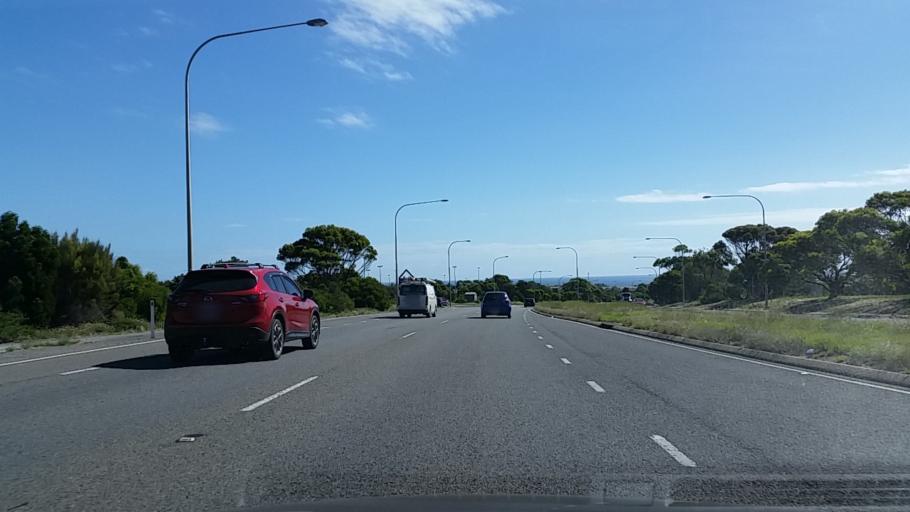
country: AU
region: South Australia
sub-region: Onkaparinga
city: Reynella
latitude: -35.0841
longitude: 138.5100
